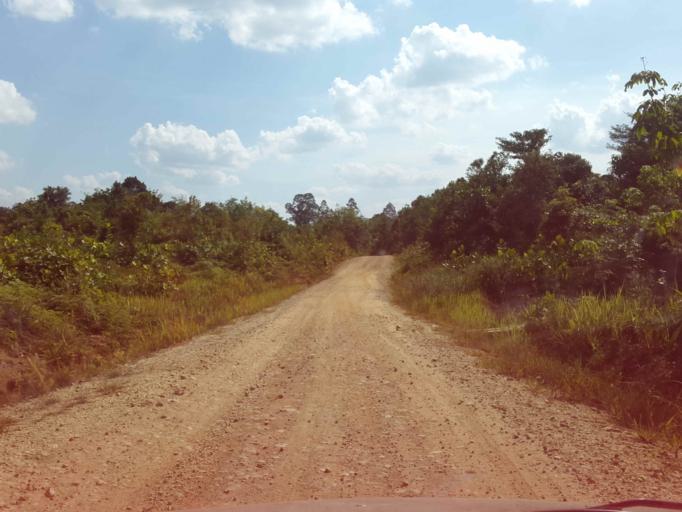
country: MY
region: Sarawak
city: Simanggang
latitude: 0.7174
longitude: 111.5428
